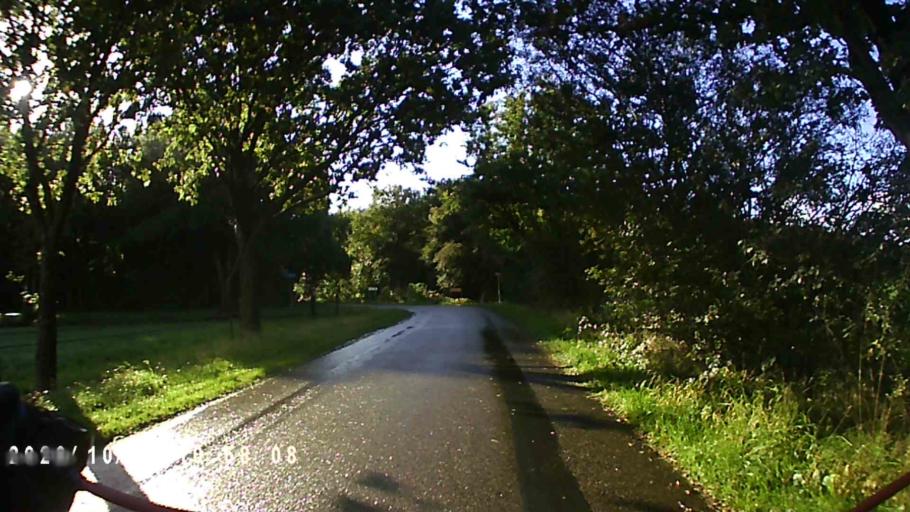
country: NL
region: Friesland
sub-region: Gemeente Achtkarspelen
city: Surhuisterveen
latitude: 53.1458
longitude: 6.2064
